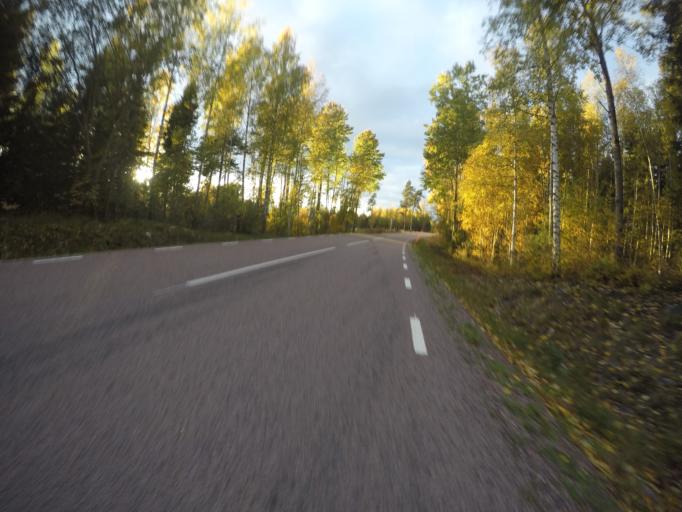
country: SE
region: Vaestmanland
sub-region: Arboga Kommun
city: Tyringe
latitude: 59.3075
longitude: 15.9985
